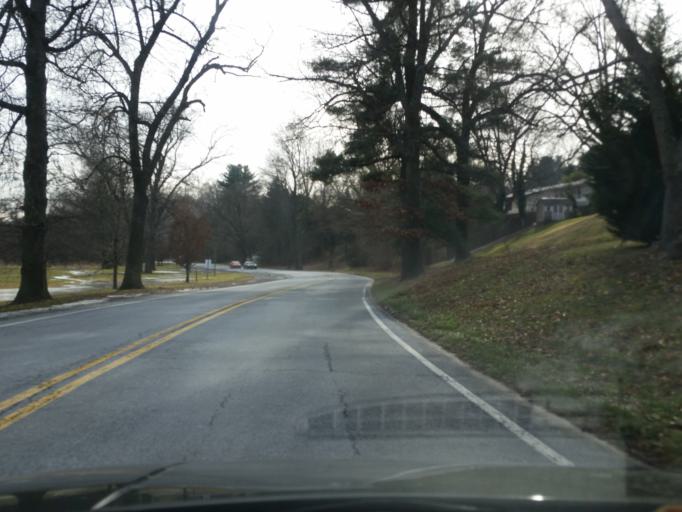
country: US
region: Maryland
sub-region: Montgomery County
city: Chevy Chase
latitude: 38.9913
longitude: -77.0635
